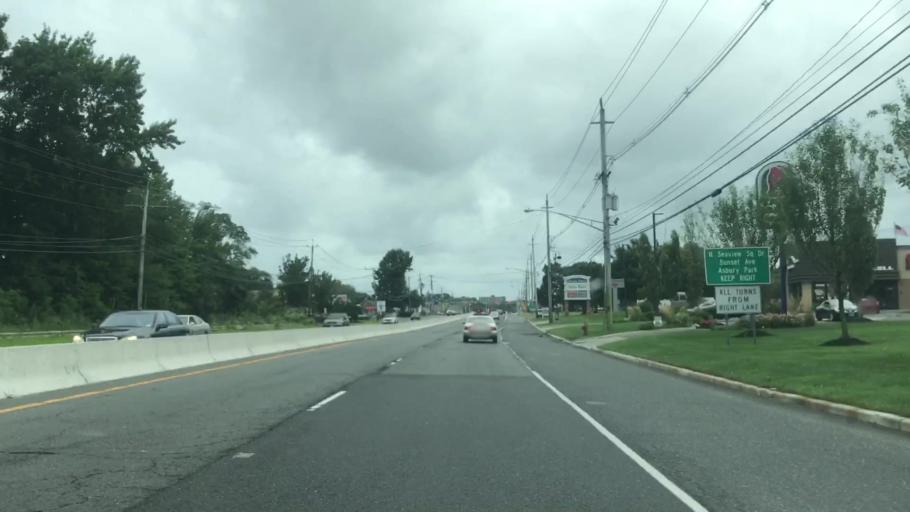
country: US
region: New Jersey
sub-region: Monmouth County
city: Wanamassa
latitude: 40.2389
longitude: -74.0374
